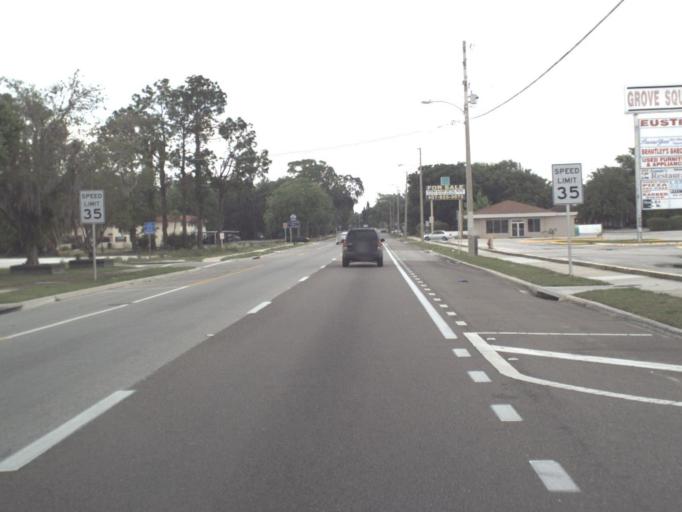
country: US
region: Florida
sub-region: Lake County
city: Eustis
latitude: 28.8567
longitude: -81.6836
